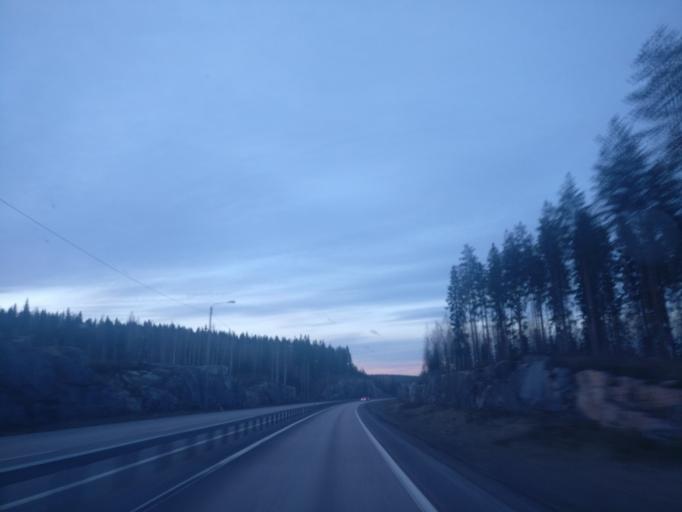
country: FI
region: Central Finland
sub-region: Jyvaeskylae
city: Saeynaetsalo
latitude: 62.2126
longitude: 25.8899
